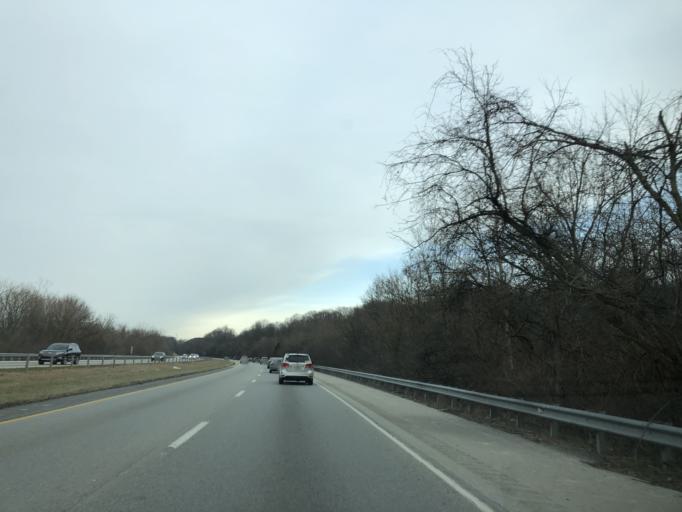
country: US
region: Pennsylvania
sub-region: Chester County
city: Exton
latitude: 40.0131
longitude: -75.6478
